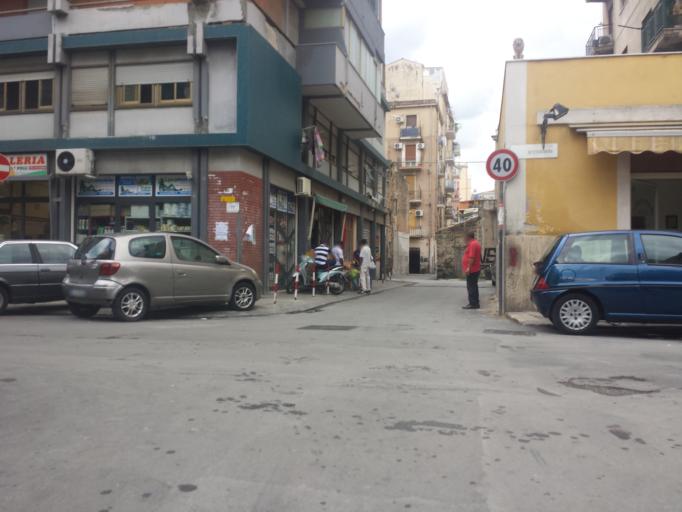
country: IT
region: Sicily
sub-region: Palermo
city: Palermo
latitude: 38.1296
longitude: 13.3566
